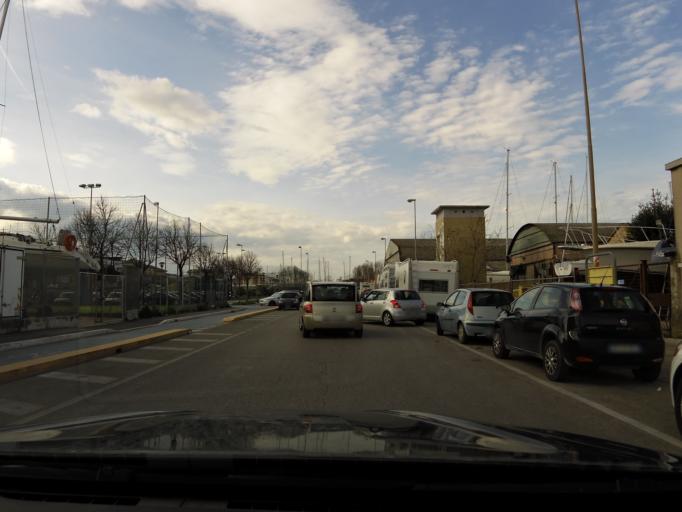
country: IT
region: The Marches
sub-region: Provincia di Macerata
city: Portocivitanova
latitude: 43.3105
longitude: 13.7295
